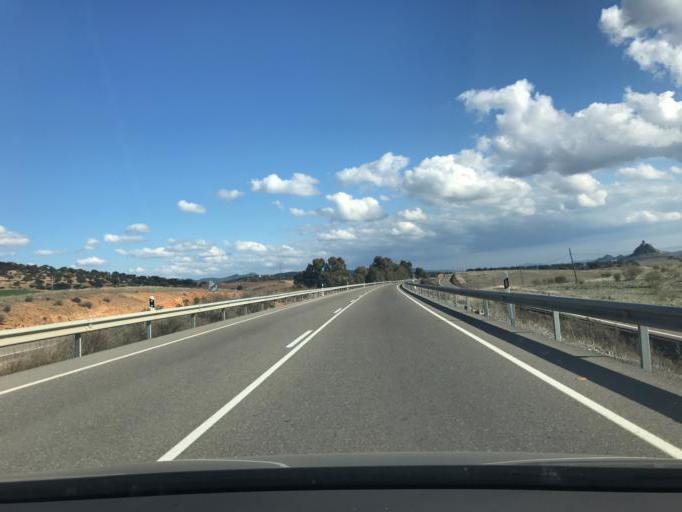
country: ES
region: Andalusia
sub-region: Province of Cordoba
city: Penarroya-Pueblonuevo
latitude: 38.2949
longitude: -5.2366
